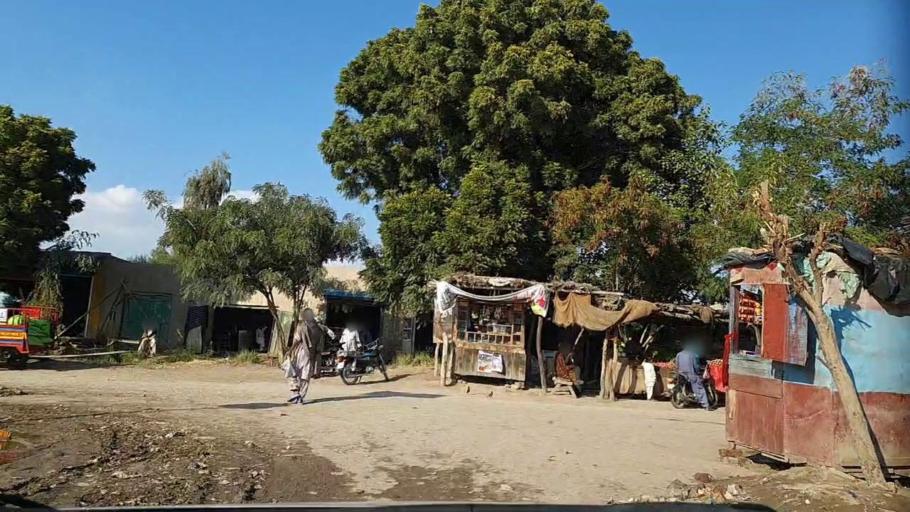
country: PK
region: Sindh
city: Pithoro
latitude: 25.6459
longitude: 69.3481
